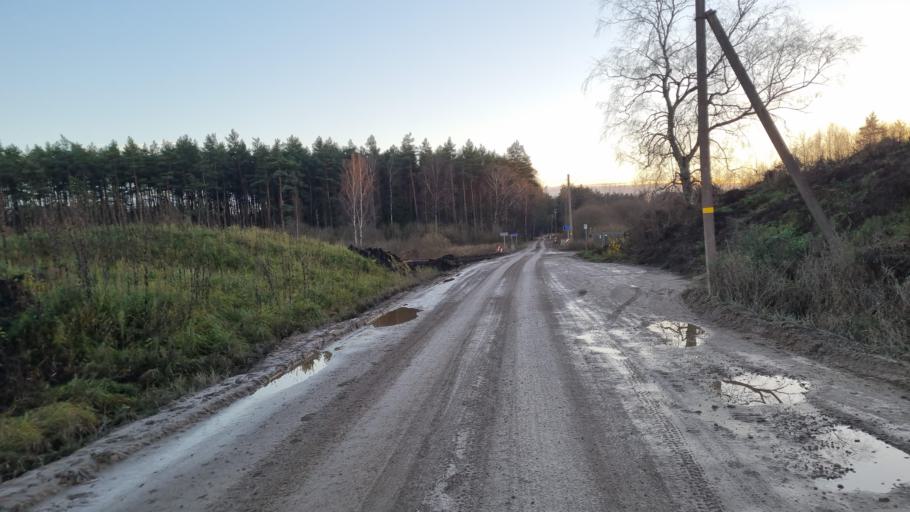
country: LV
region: Kekava
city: Balozi
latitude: 56.8644
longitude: 24.1651
